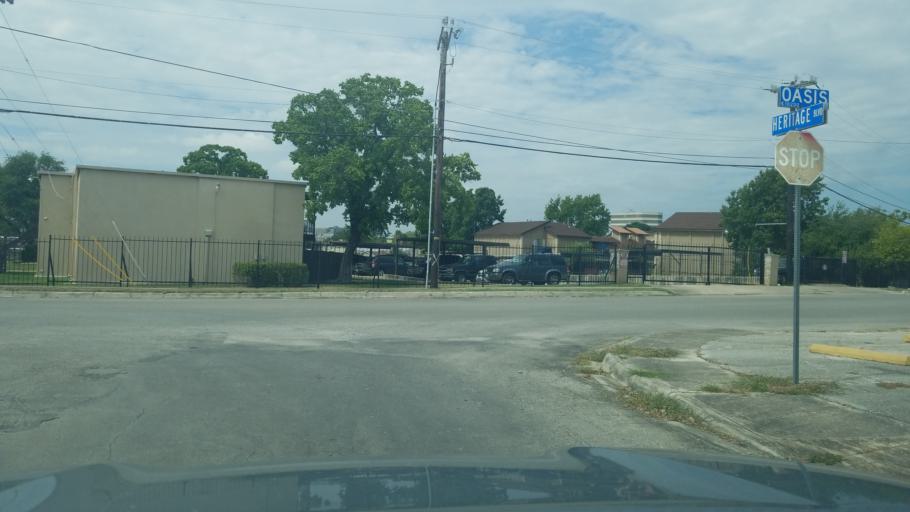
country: US
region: Texas
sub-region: Bexar County
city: Castle Hills
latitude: 29.5331
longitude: -98.4898
